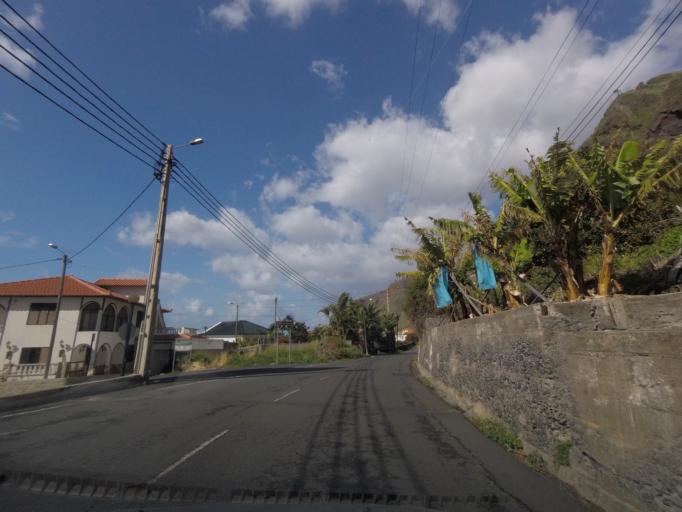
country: PT
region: Madeira
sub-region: Calheta
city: Faja da Ovelha
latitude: 32.7546
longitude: -17.2263
